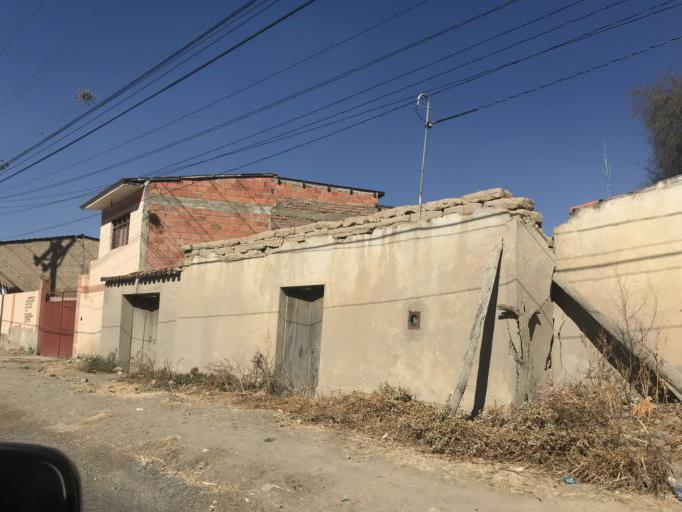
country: BO
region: Cochabamba
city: Punata
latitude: -17.5619
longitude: -65.8768
